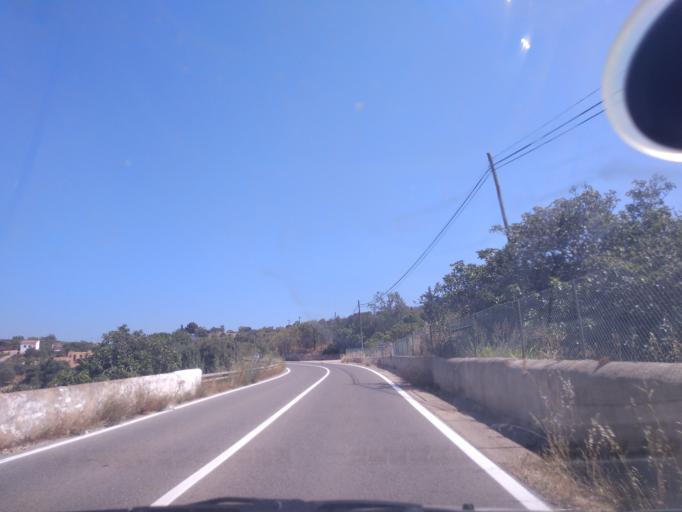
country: PT
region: Faro
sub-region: Lagos
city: Lagos
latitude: 37.1199
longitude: -8.6927
